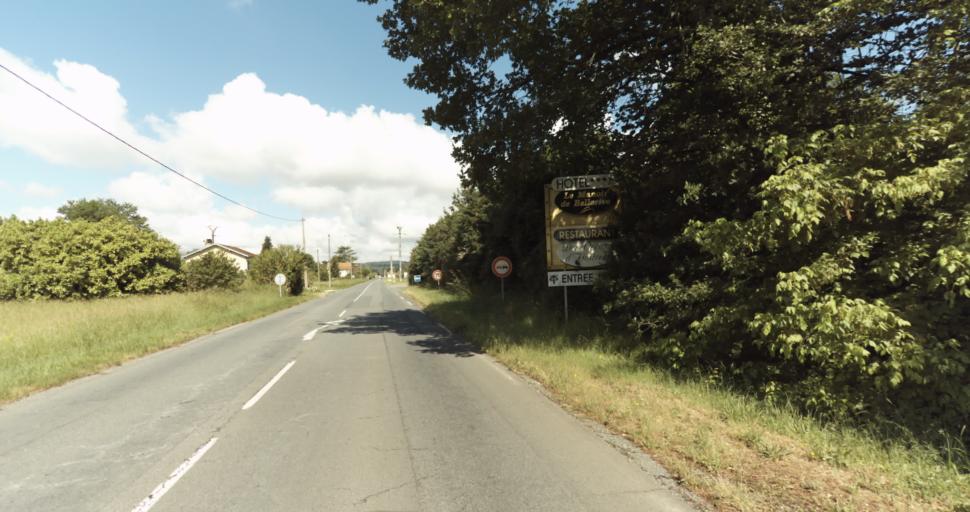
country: FR
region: Aquitaine
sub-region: Departement de la Dordogne
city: Le Bugue
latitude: 44.8434
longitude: 0.9251
